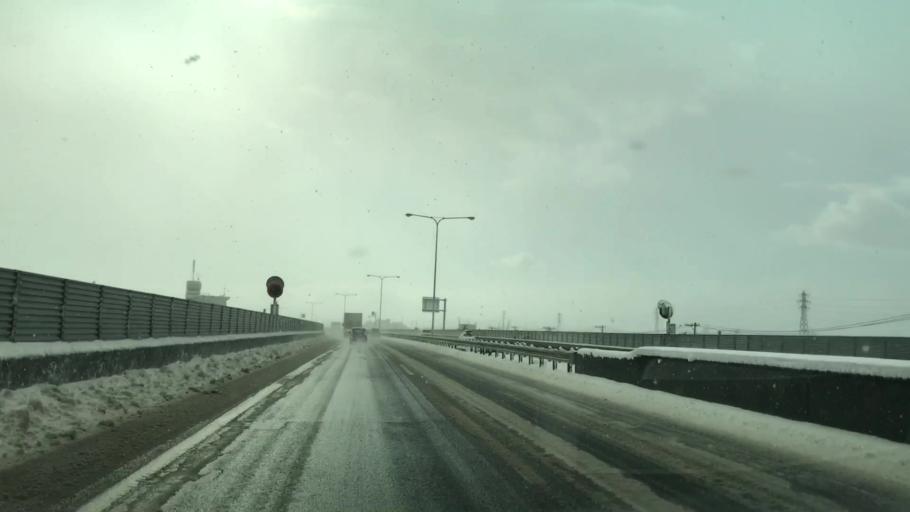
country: JP
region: Hokkaido
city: Sapporo
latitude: 43.0624
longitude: 141.4243
